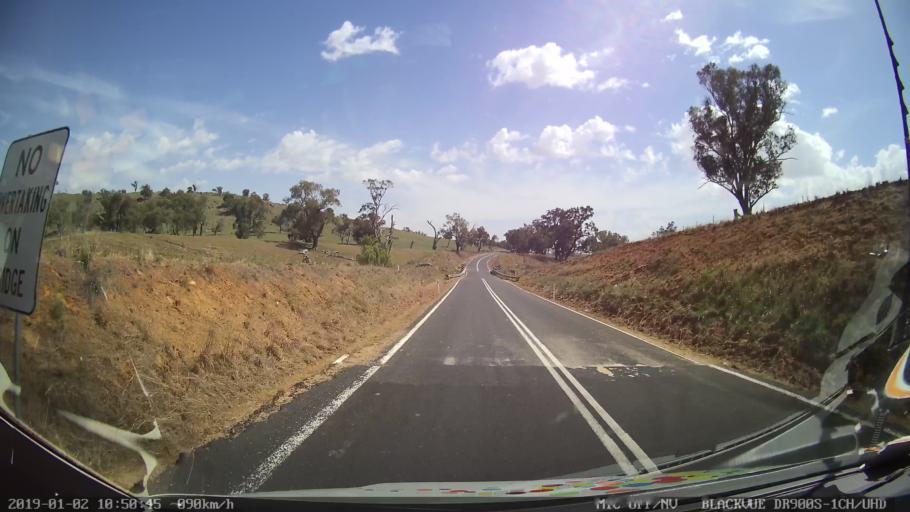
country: AU
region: New South Wales
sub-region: Cootamundra
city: Cootamundra
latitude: -34.7100
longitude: 148.2756
